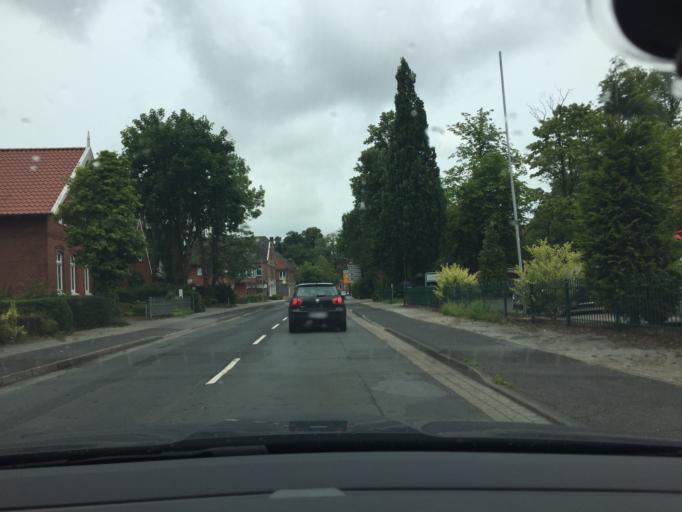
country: DE
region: Lower Saxony
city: Aurich
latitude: 53.4656
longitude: 7.4810
